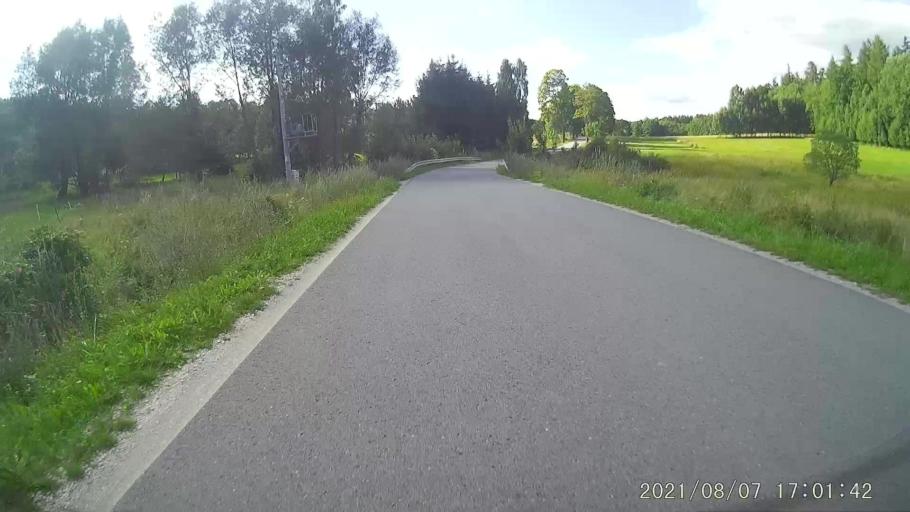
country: PL
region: Lower Silesian Voivodeship
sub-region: Powiat klodzki
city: Bystrzyca Klodzka
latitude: 50.2856
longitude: 16.5554
